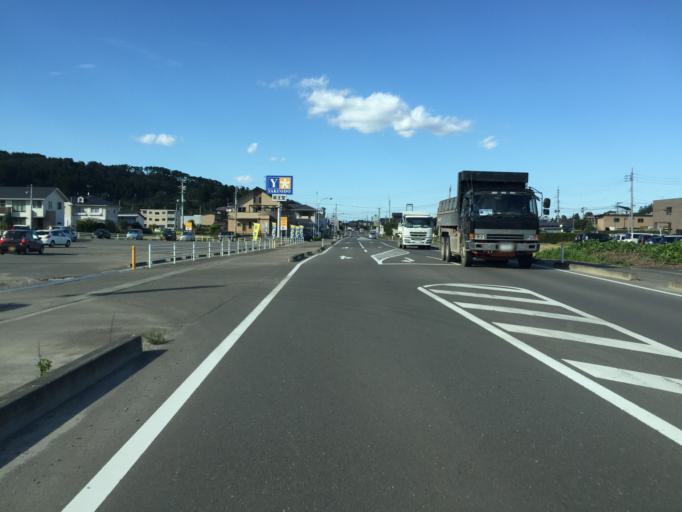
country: JP
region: Miyagi
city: Marumori
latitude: 37.9100
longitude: 140.7641
